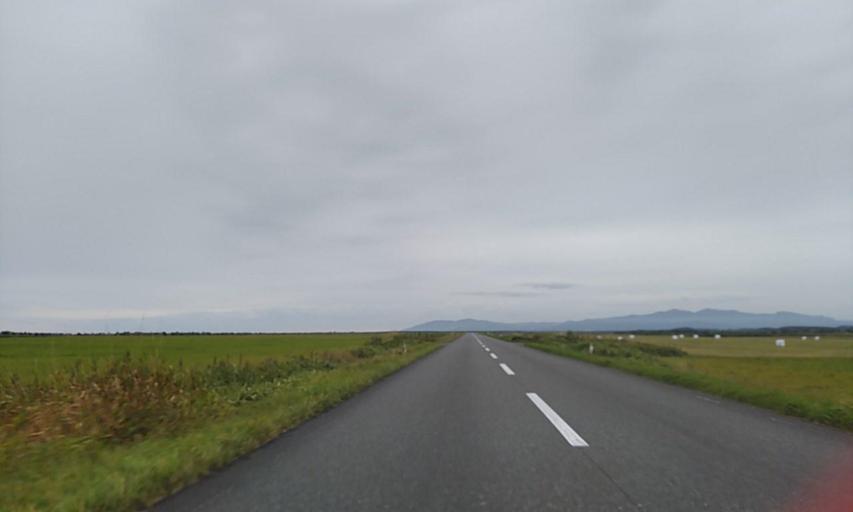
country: JP
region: Hokkaido
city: Makubetsu
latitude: 45.2013
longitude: 142.2994
